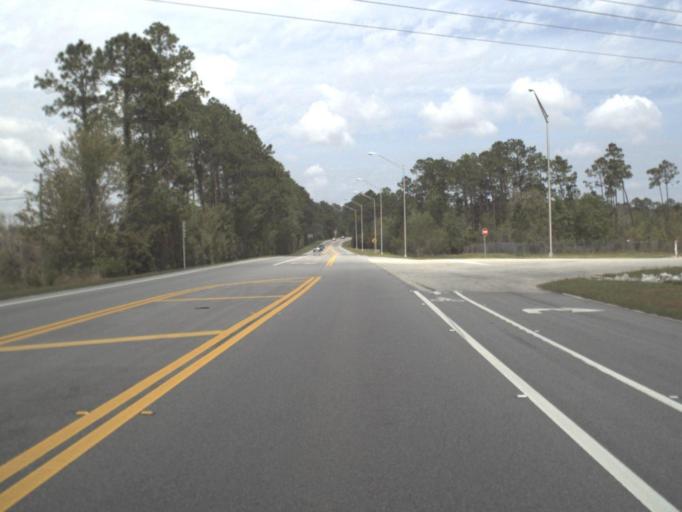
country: US
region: Florida
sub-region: Escambia County
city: Cantonment
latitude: 30.5299
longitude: -87.4291
